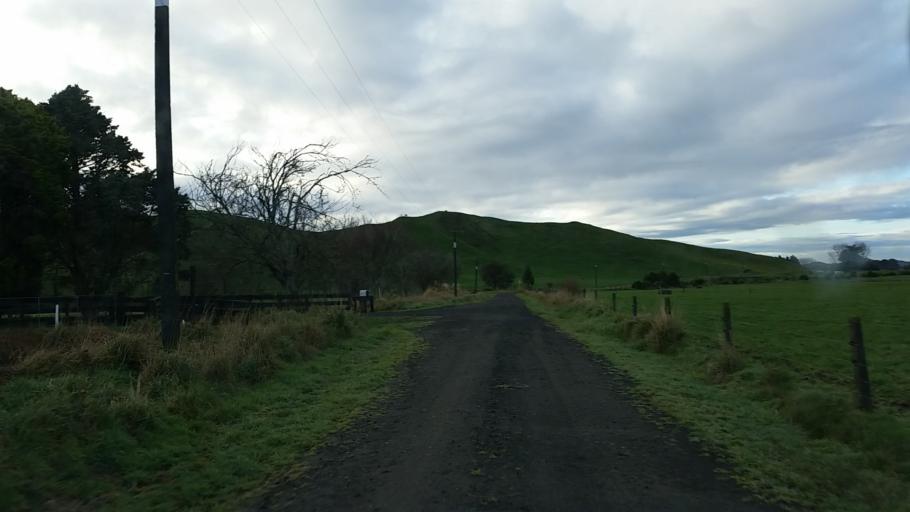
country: NZ
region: Taranaki
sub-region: South Taranaki District
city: Eltham
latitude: -39.3166
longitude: 174.3827
